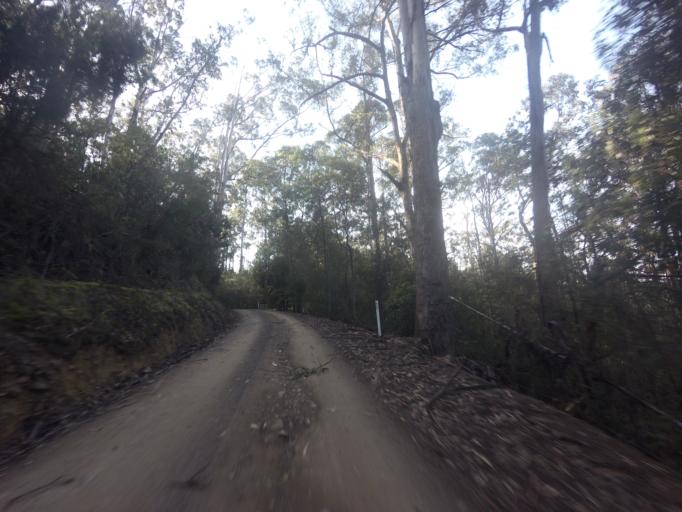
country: AU
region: Tasmania
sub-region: Kingborough
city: Kettering
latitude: -43.1060
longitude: 147.2573
